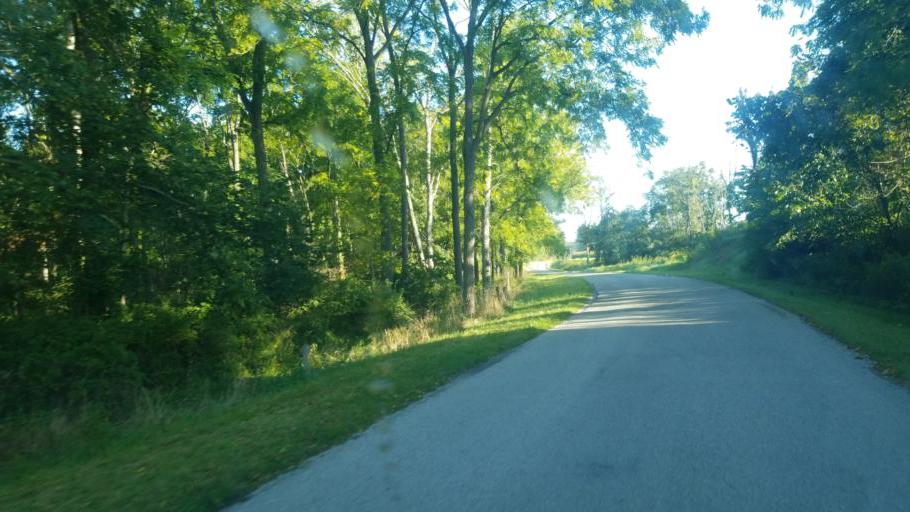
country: US
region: Ohio
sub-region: Lorain County
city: Wellington
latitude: 41.1036
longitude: -82.2787
